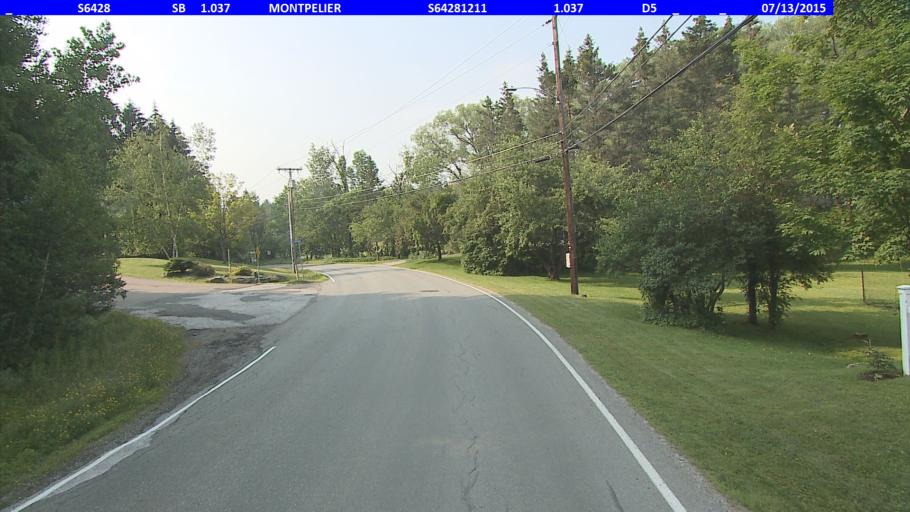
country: US
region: Vermont
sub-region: Washington County
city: Montpelier
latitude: 44.2763
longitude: -72.5938
